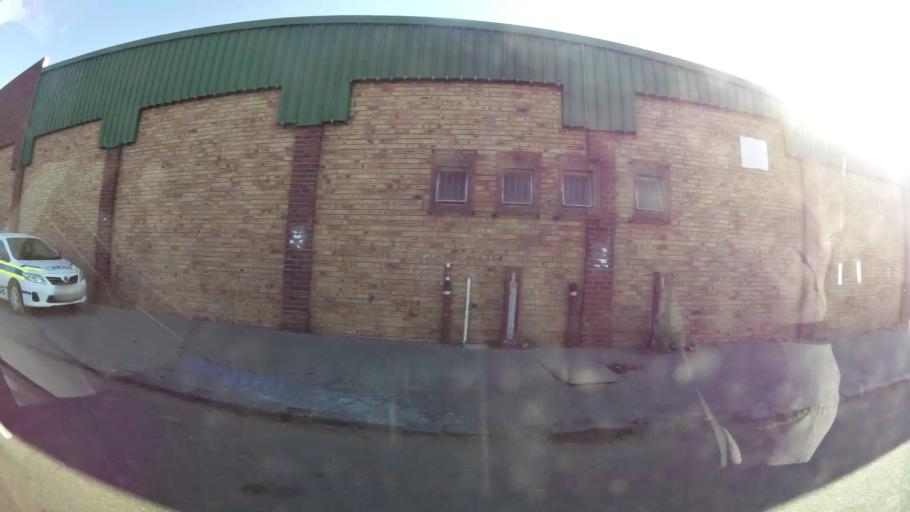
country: ZA
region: Northern Cape
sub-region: Frances Baard District Municipality
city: Kimberley
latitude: -28.7356
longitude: 24.7621
